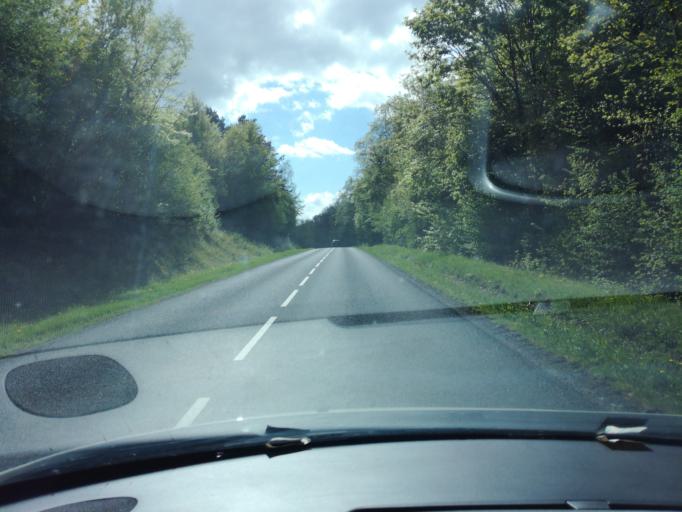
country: FR
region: Picardie
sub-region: Departement de la Somme
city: Quevauvillers
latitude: 49.8885
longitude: 2.1041
